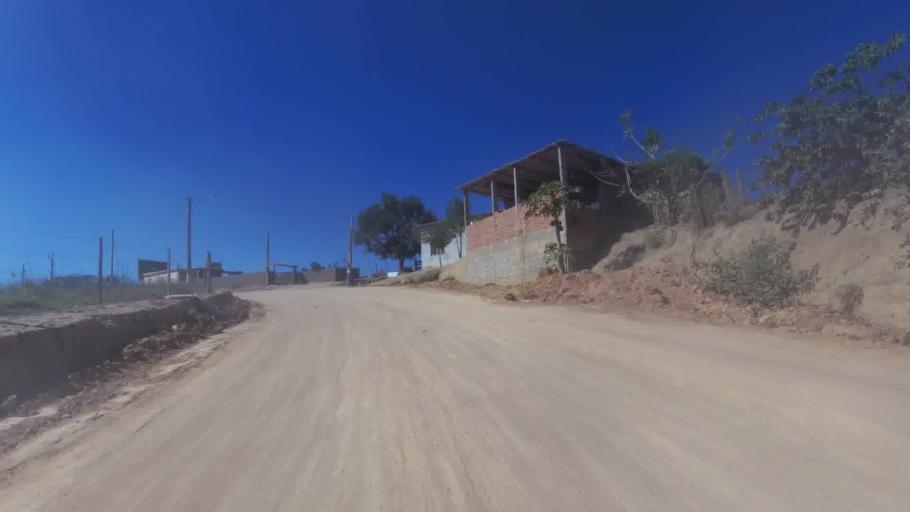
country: BR
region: Espirito Santo
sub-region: Marataizes
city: Marataizes
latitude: -21.1455
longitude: -40.9832
